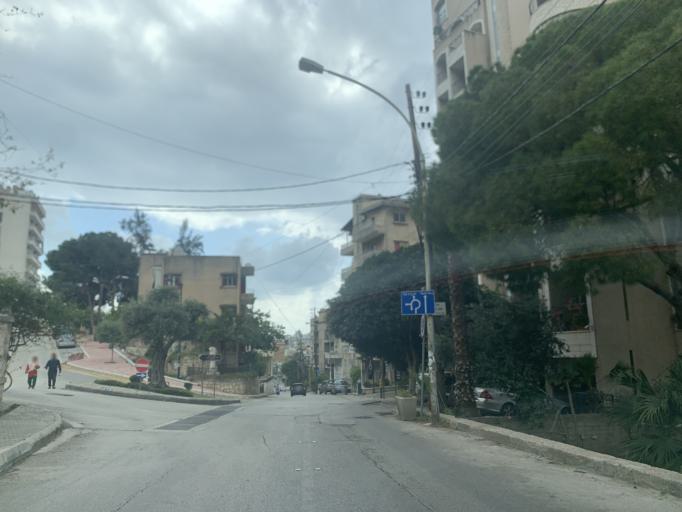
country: LB
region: Mont-Liban
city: Djounie
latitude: 33.9824
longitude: 35.6378
